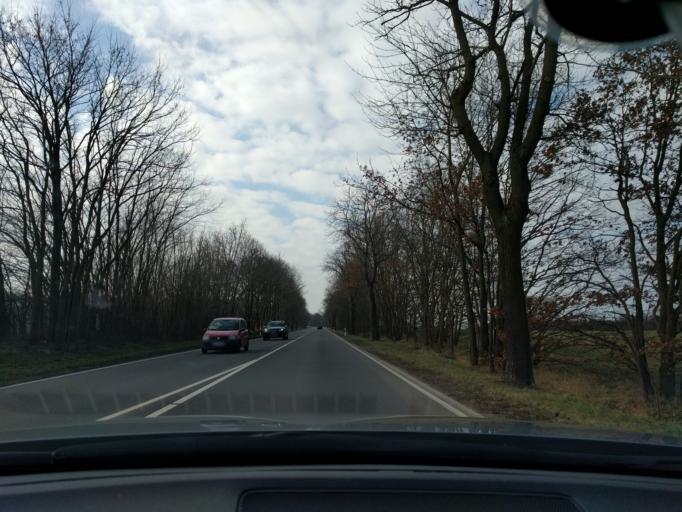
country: DE
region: Saxony-Anhalt
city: Burgstall
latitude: 52.3990
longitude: 11.6224
